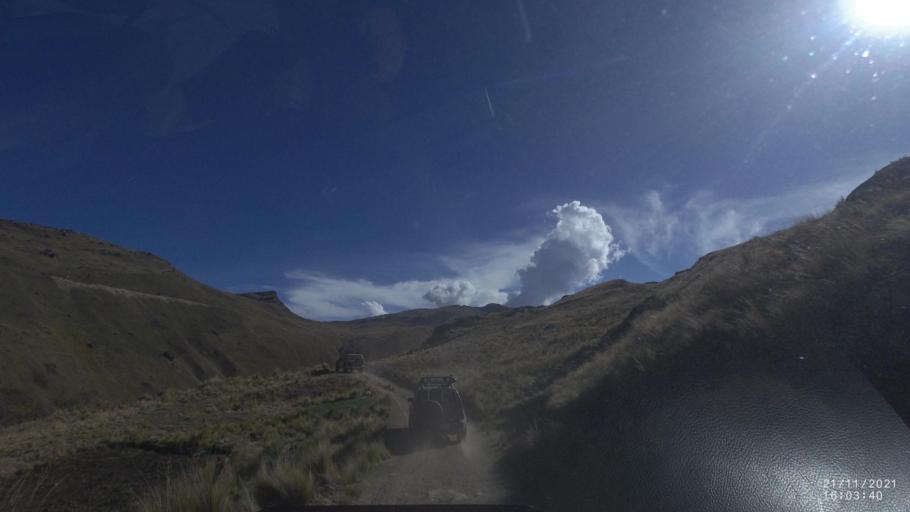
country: BO
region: Cochabamba
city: Cochabamba
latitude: -16.9882
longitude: -66.2593
